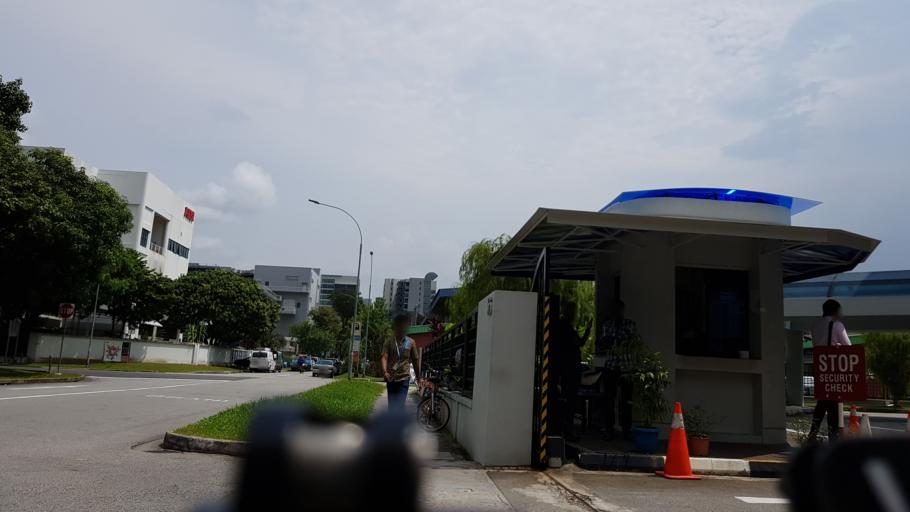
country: MY
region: Johor
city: Kampung Pasir Gudang Baru
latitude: 1.4411
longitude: 103.8349
